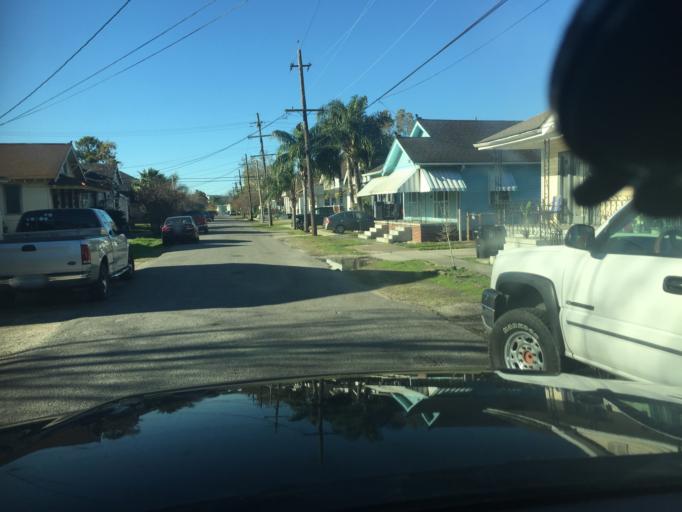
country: US
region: Louisiana
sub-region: Orleans Parish
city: New Orleans
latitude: 29.9841
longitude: -90.0730
